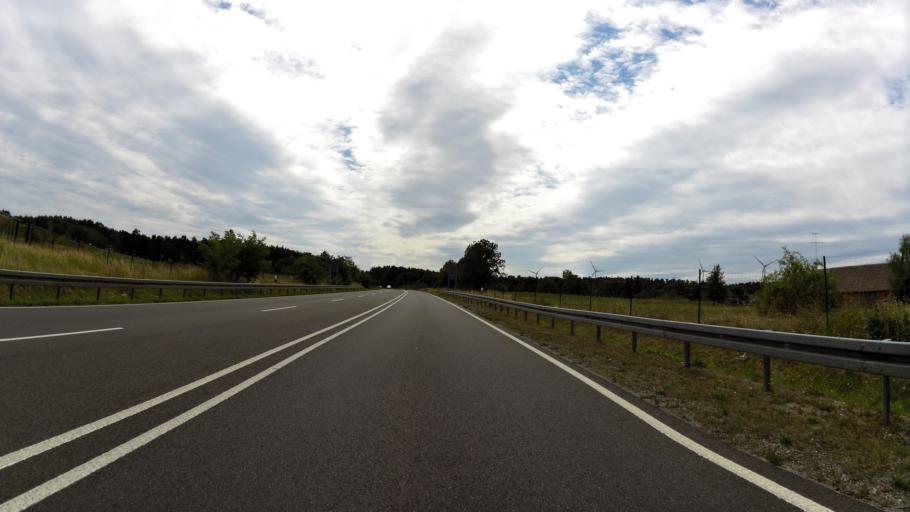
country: DE
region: Brandenburg
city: Neuzelle
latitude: 52.0259
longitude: 14.6769
